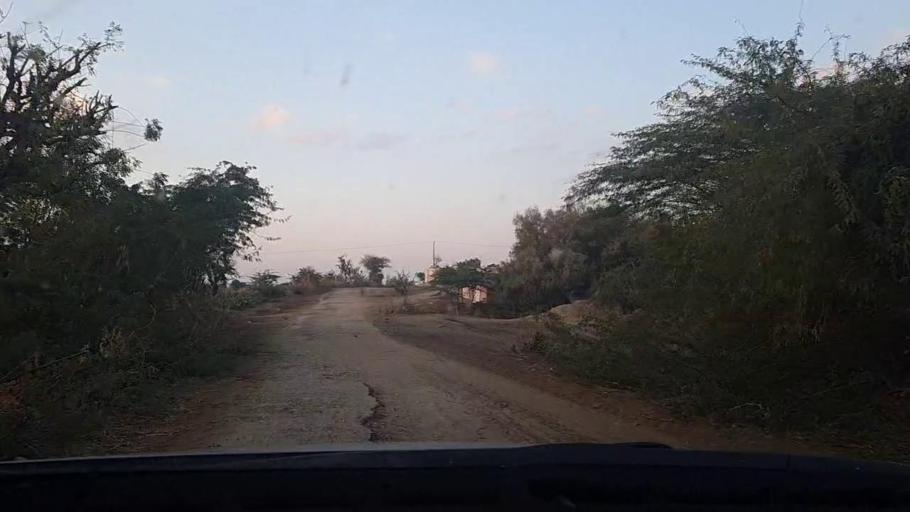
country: PK
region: Sindh
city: Tando Mittha Khan
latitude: 25.9421
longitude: 69.3383
